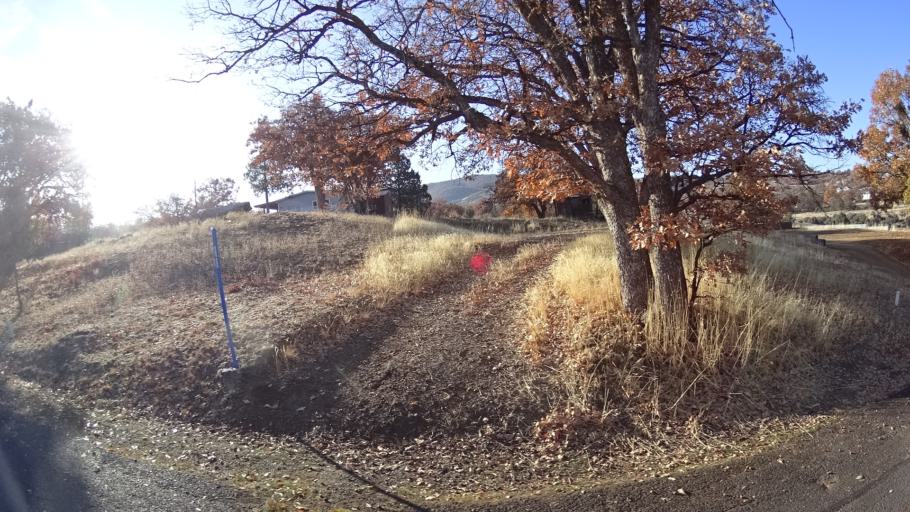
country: US
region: California
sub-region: Siskiyou County
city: Yreka
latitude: 41.7068
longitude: -122.6174
